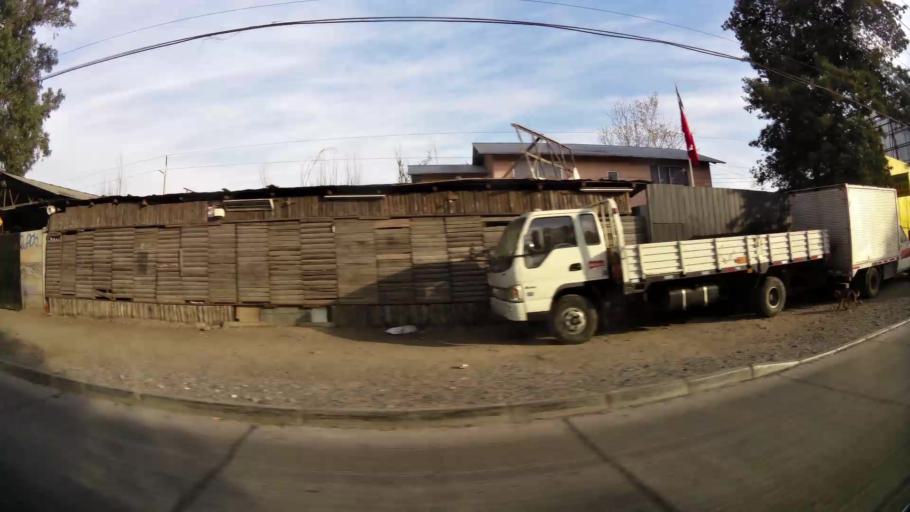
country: CL
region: Santiago Metropolitan
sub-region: Provincia de Talagante
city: Penaflor
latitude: -33.5565
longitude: -70.7995
